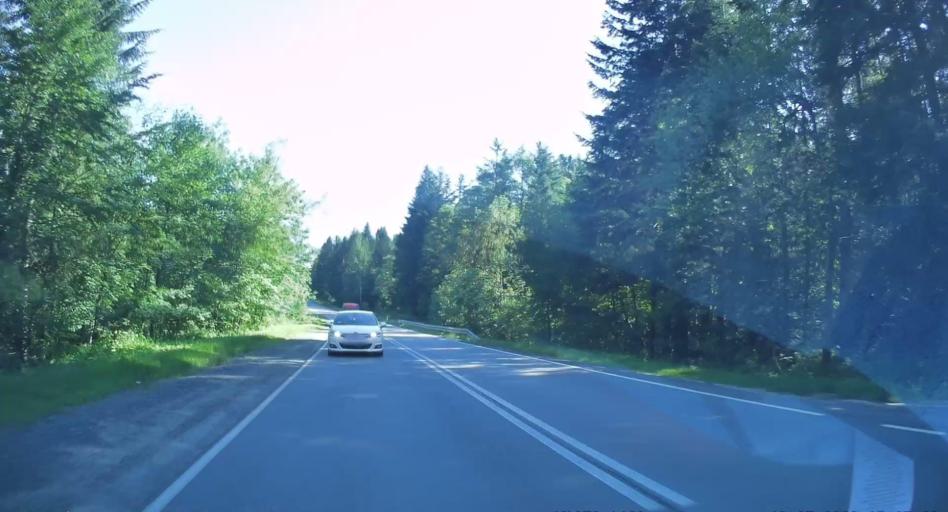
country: PL
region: Lesser Poland Voivodeship
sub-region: Powiat nowosadecki
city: Krynica-Zdroj
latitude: 49.4548
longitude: 20.9525
